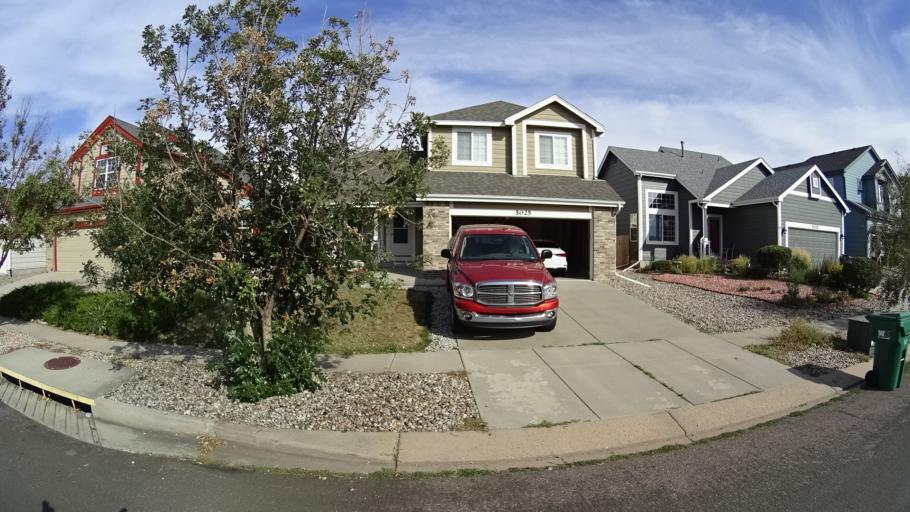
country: US
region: Colorado
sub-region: El Paso County
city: Cimarron Hills
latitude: 38.9069
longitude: -104.6920
